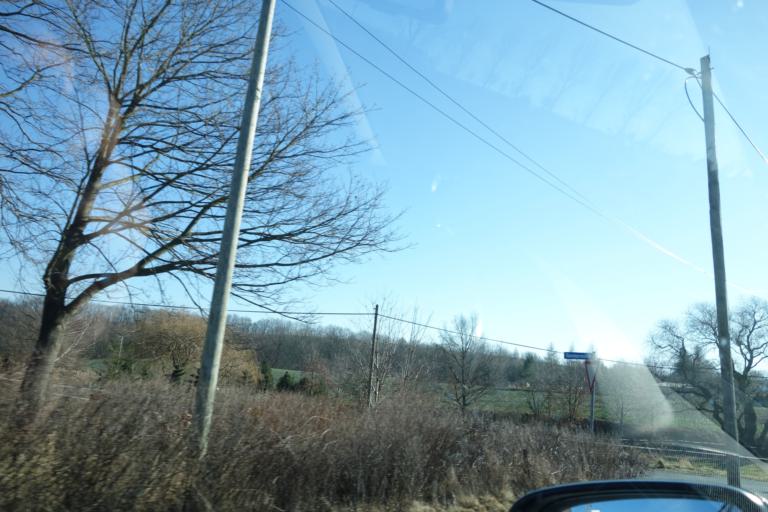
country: DE
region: Saxony
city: Frankenstein
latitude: 50.9463
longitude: 13.1829
